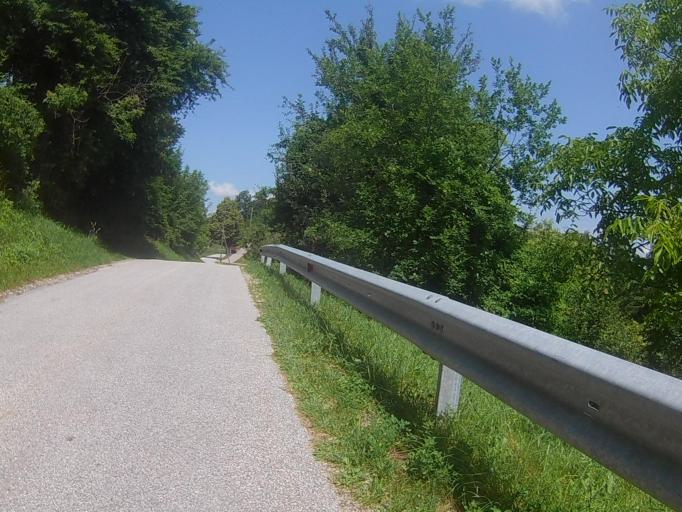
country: SI
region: Maribor
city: Kamnica
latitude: 46.6044
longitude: 15.6057
